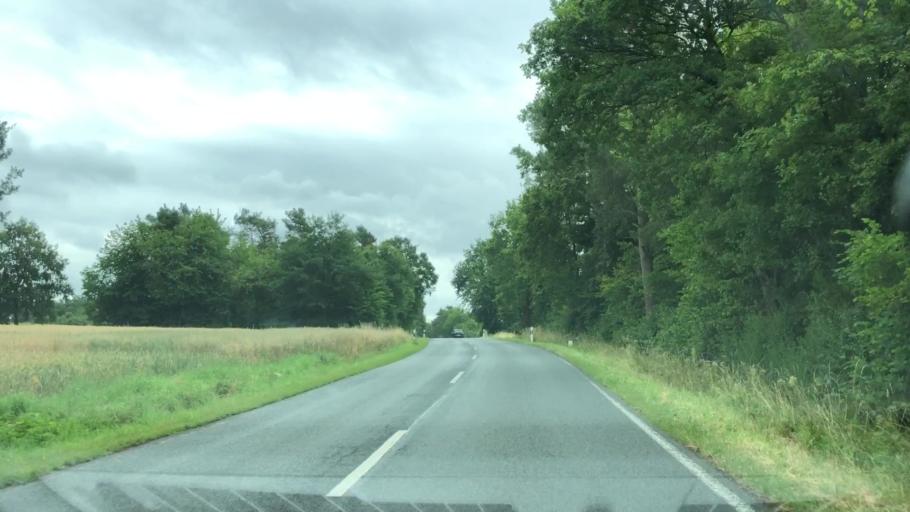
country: DE
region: Hesse
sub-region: Regierungsbezirk Darmstadt
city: Steinau an der Strasse
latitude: 50.3038
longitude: 9.4808
